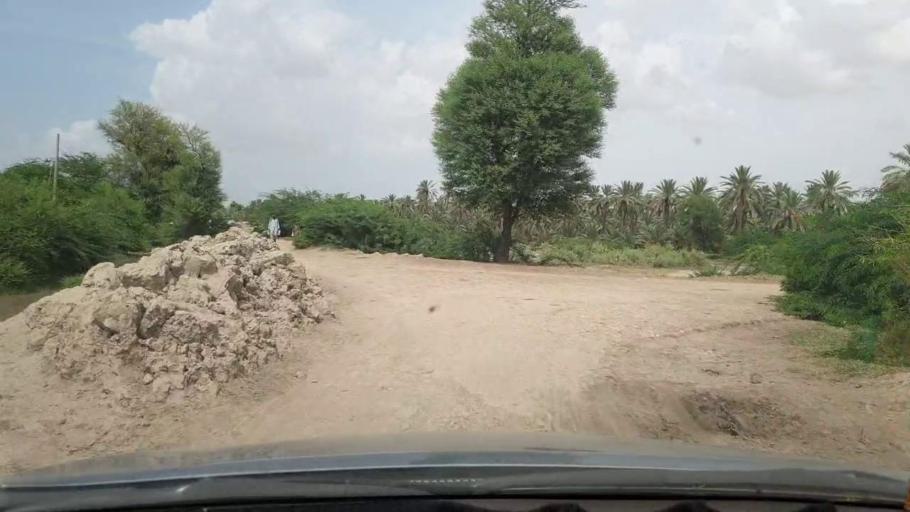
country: PK
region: Sindh
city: Khairpur
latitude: 27.4739
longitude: 68.8493
